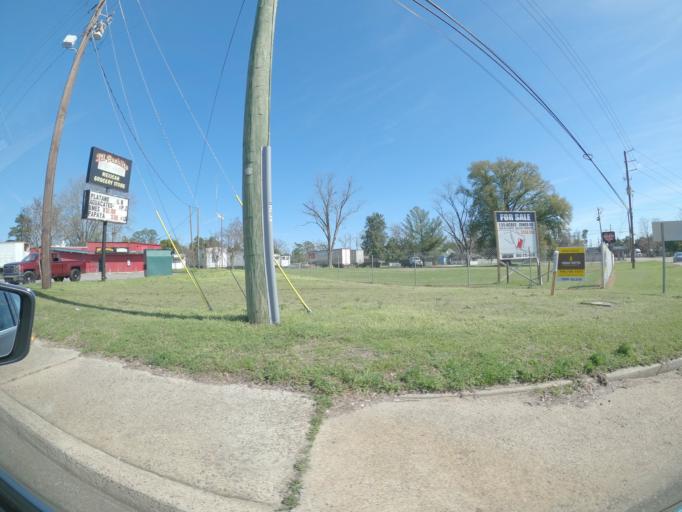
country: US
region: South Carolina
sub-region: Aiken County
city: North Augusta
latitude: 33.4856
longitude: -81.9487
